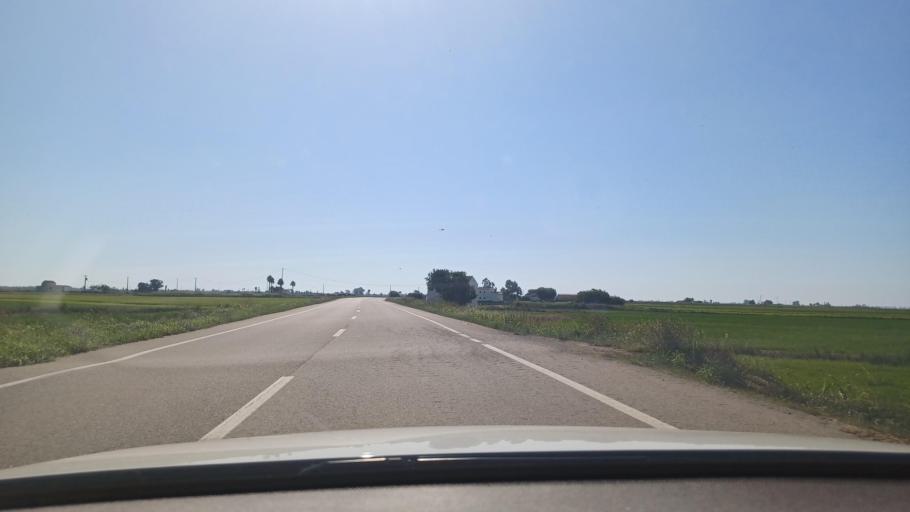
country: ES
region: Catalonia
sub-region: Provincia de Tarragona
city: Deltebre
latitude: 40.7021
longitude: 0.6684
